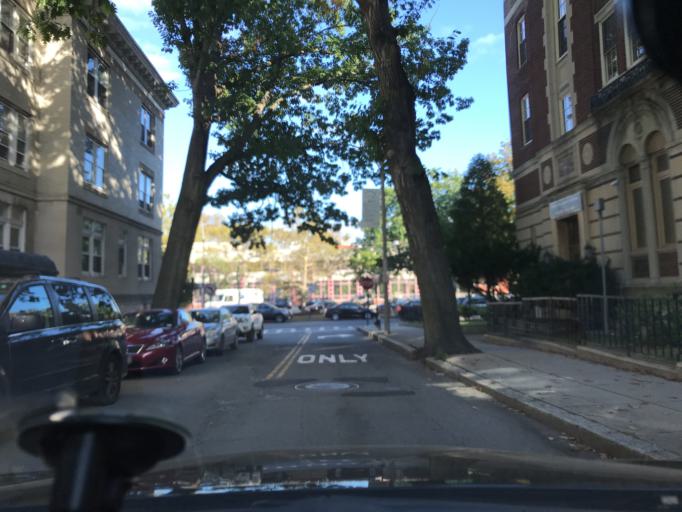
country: US
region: Massachusetts
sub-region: Norfolk County
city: Brookline
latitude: 42.3431
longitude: -71.1150
